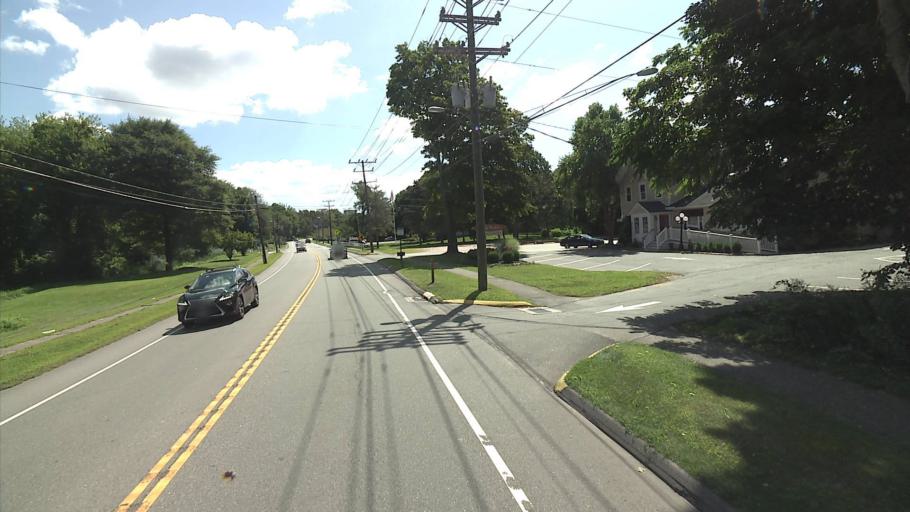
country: US
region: Connecticut
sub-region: Middlesex County
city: Westbrook Center
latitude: 41.2838
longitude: -72.4439
